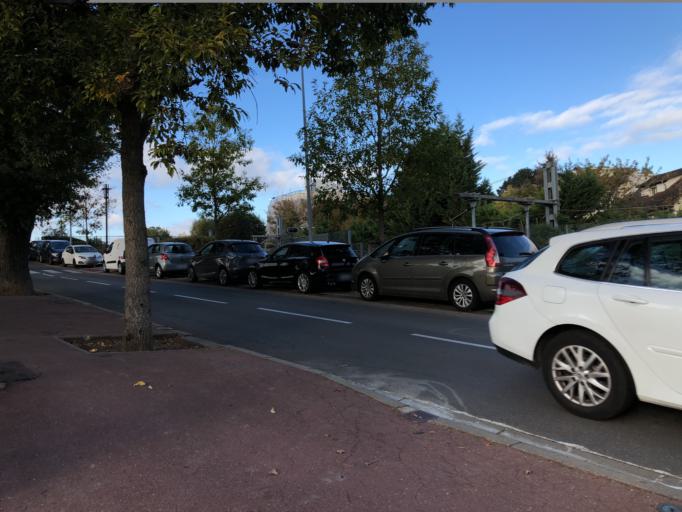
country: FR
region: Ile-de-France
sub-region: Departement des Hauts-de-Seine
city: Chaville
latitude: 48.8057
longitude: 2.1787
